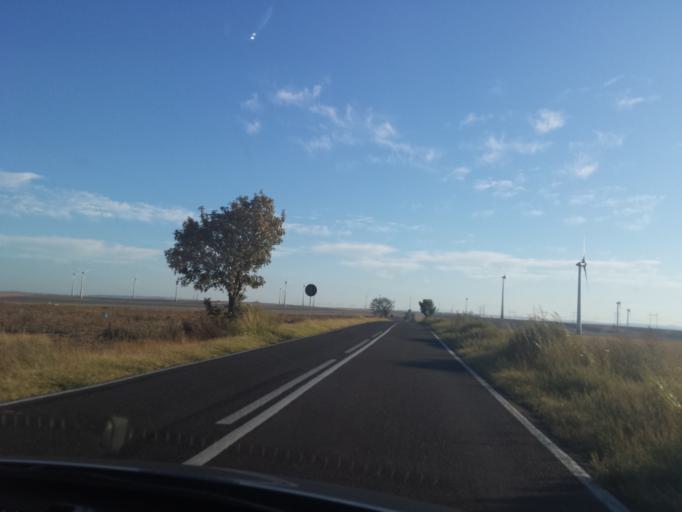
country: RO
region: Constanta
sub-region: Comuna Saraiu
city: Saraiu
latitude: 44.7812
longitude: 28.2287
